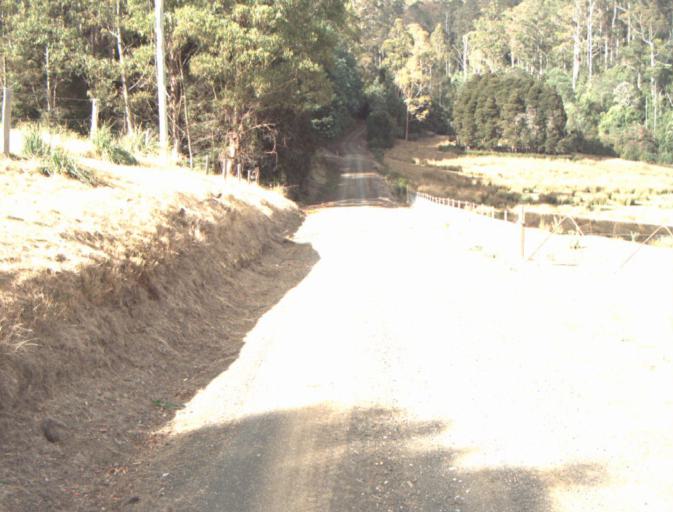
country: AU
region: Tasmania
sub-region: Launceston
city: Mayfield
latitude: -41.2950
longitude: 147.2152
